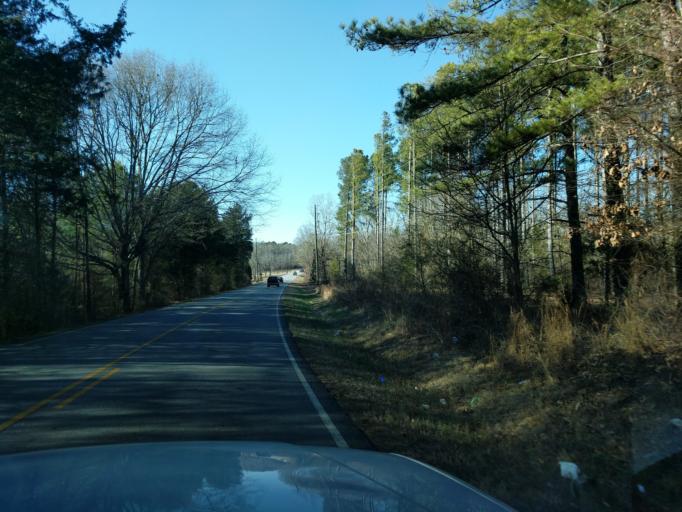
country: US
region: Georgia
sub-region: Hart County
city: Hartwell
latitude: 34.3292
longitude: -82.8960
